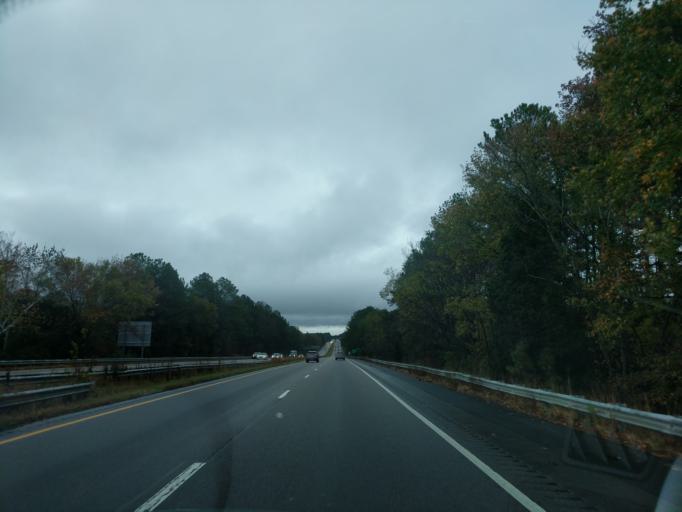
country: US
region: North Carolina
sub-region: Durham County
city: Gorman
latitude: 36.0486
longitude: -78.8107
